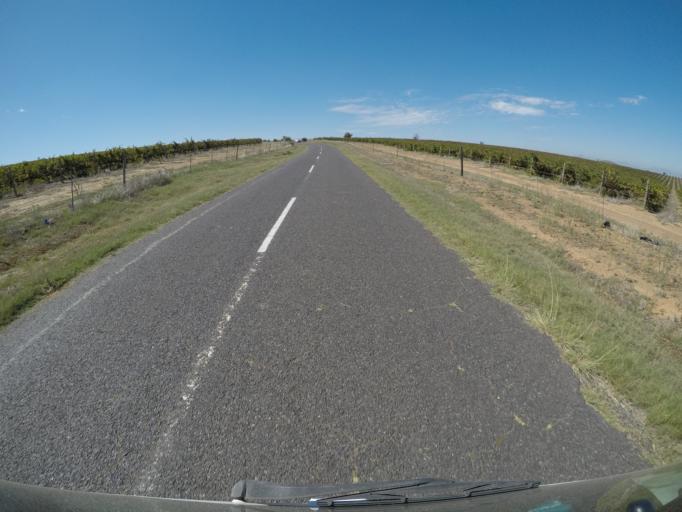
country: ZA
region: Western Cape
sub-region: City of Cape Town
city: Sunset Beach
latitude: -33.7179
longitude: 18.5796
